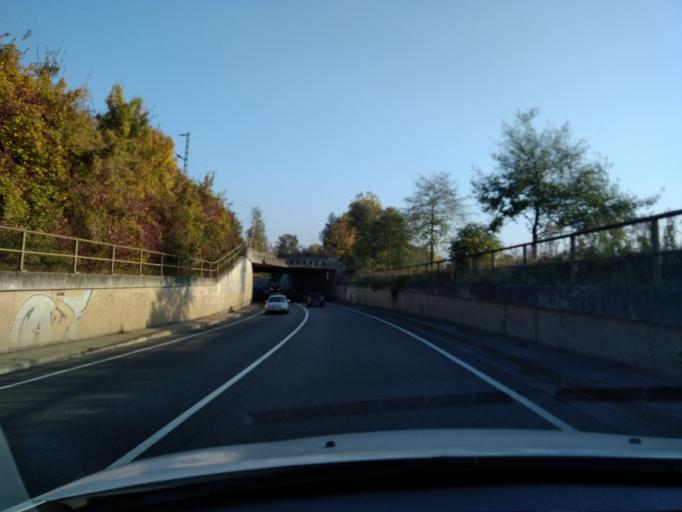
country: DE
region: Saarland
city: Kleinblittersdorf
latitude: 49.1533
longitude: 7.0356
